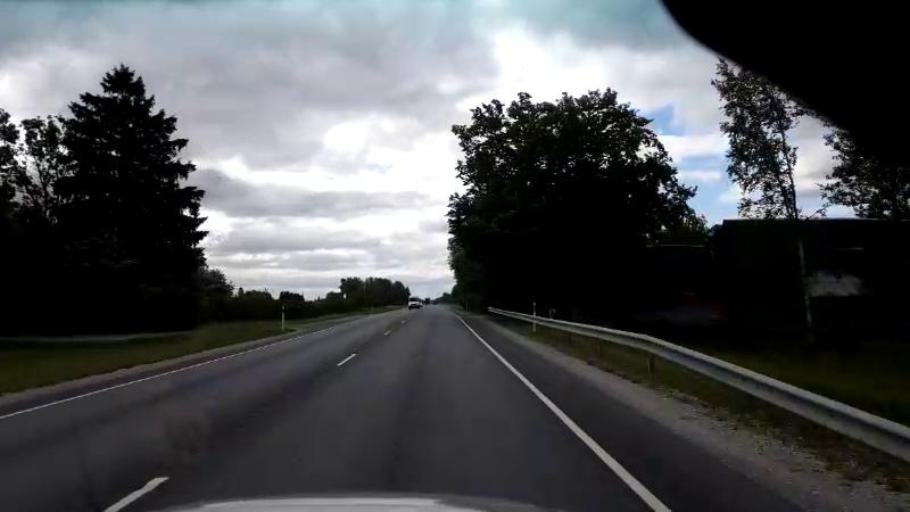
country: EE
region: Paernumaa
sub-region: Halinga vald
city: Parnu-Jaagupi
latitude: 58.6504
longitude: 24.4804
